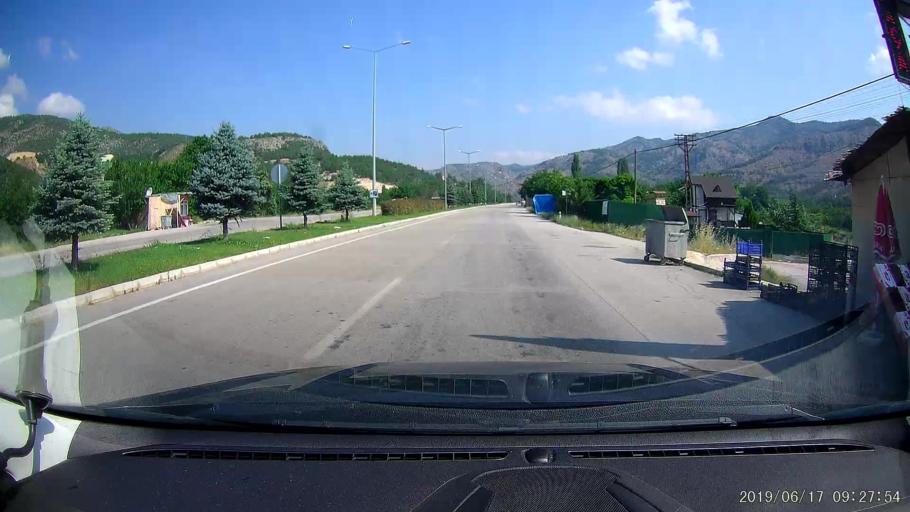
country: TR
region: Amasya
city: Amasya
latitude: 40.6821
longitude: 35.8238
